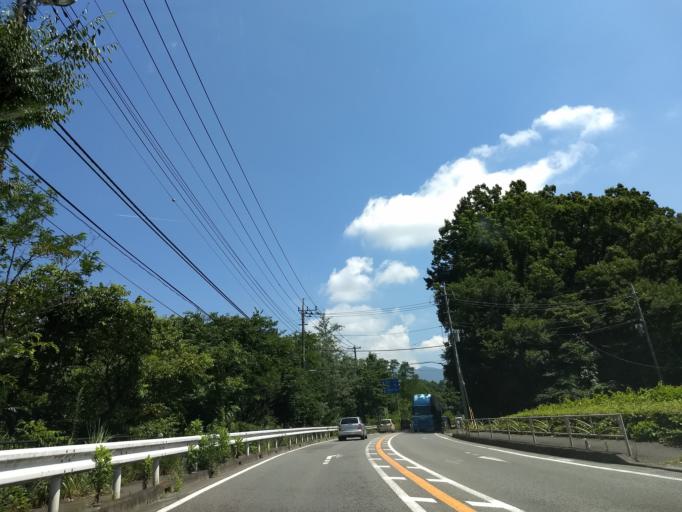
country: JP
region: Kanagawa
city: Hadano
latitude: 35.3637
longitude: 139.1587
